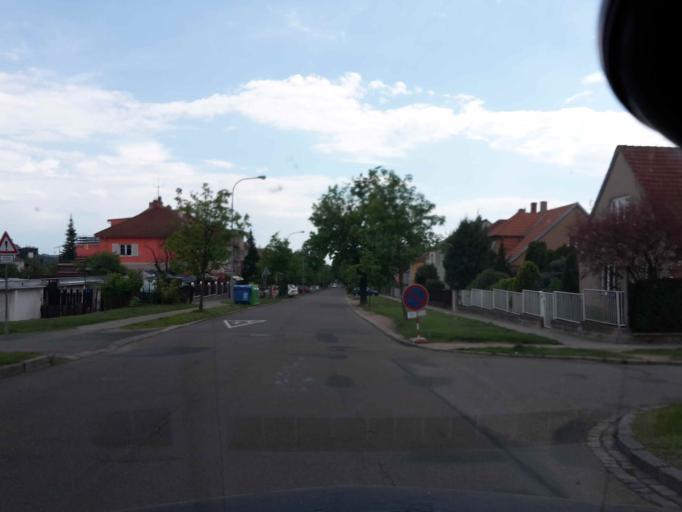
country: CZ
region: South Moravian
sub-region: Mesto Brno
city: Brno
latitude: 49.2236
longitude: 16.6327
